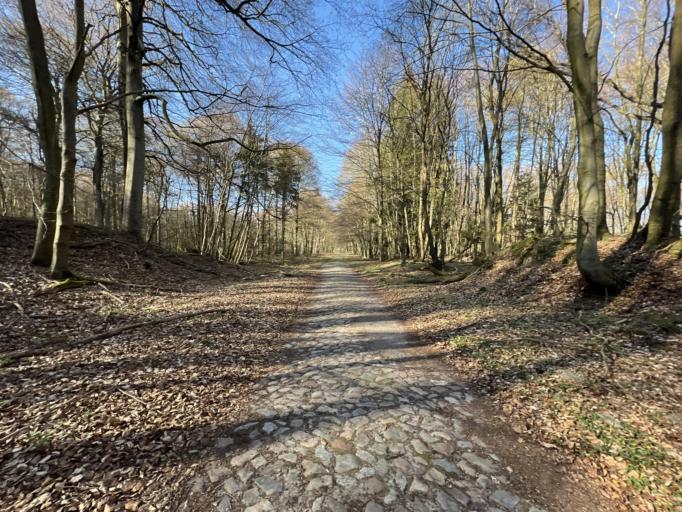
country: DE
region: Mecklenburg-Vorpommern
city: Sassnitz
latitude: 54.5315
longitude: 13.6430
